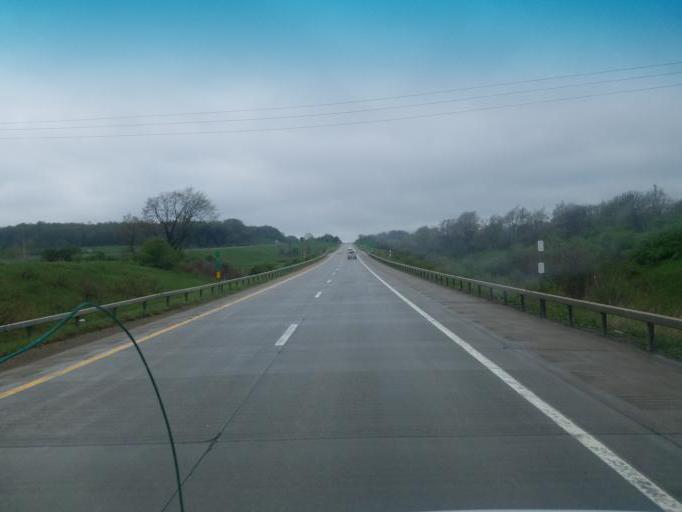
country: US
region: New York
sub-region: Chautauqua County
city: Clymer
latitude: 42.1467
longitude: -79.6107
